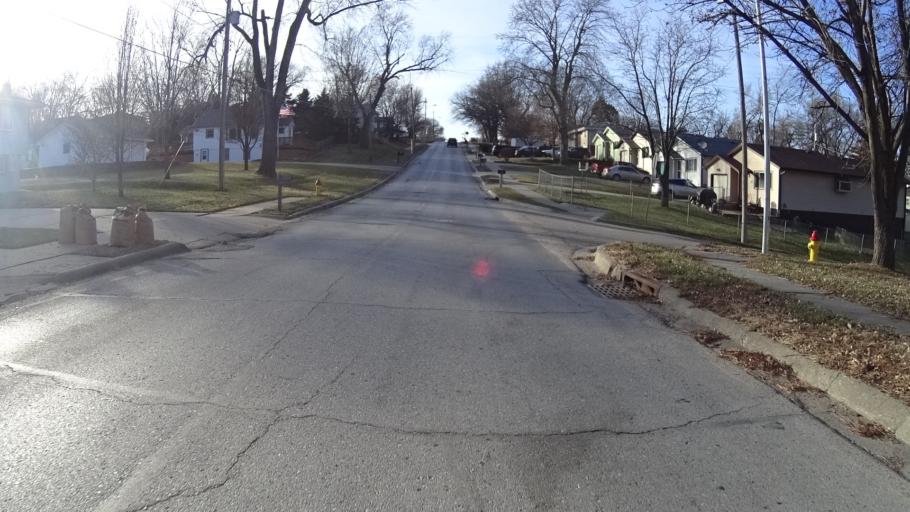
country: US
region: Nebraska
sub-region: Douglas County
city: Omaha
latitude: 41.1909
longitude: -95.9597
